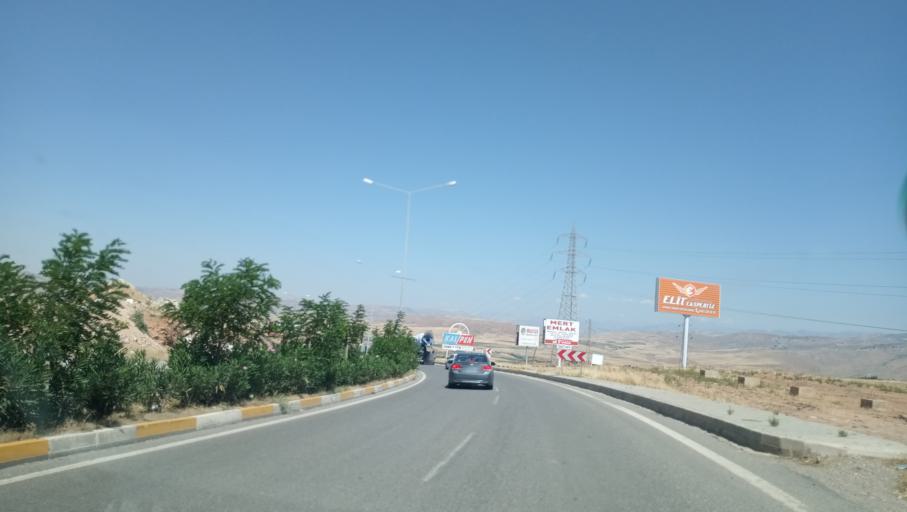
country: TR
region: Siirt
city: Civankan
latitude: 37.9523
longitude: 41.8892
